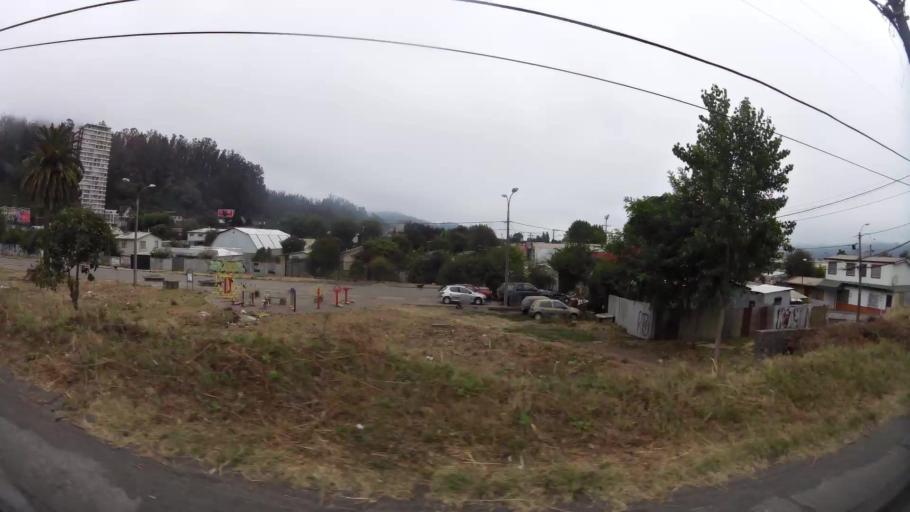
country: CL
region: Biobio
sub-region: Provincia de Concepcion
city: Concepcion
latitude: -36.8362
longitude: -73.0583
